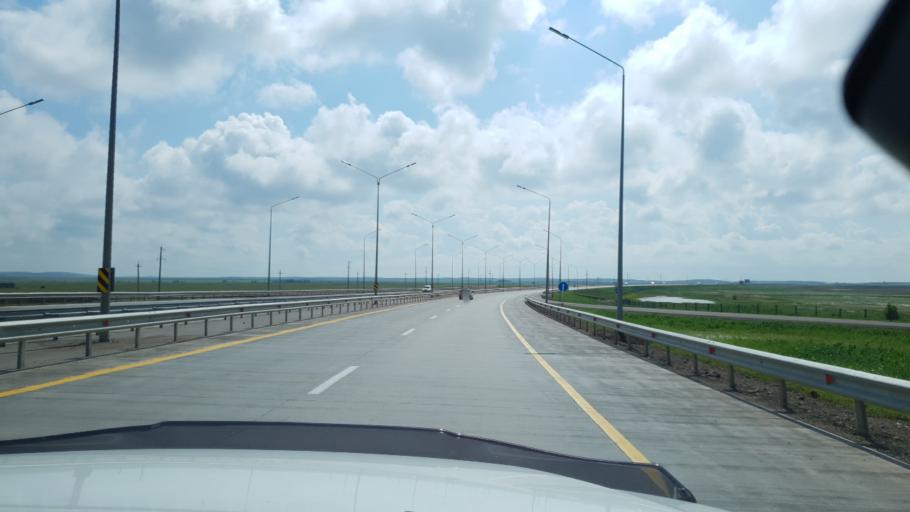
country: KZ
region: Qaraghandy
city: Osakarovka
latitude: 50.8111
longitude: 72.1890
